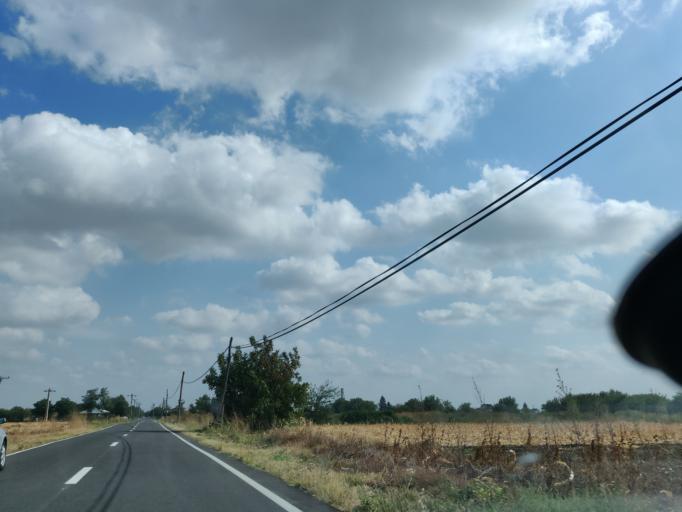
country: RO
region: Vrancea
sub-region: Comuna Ciorasti
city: Ciorasti
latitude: 45.4253
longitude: 27.2869
